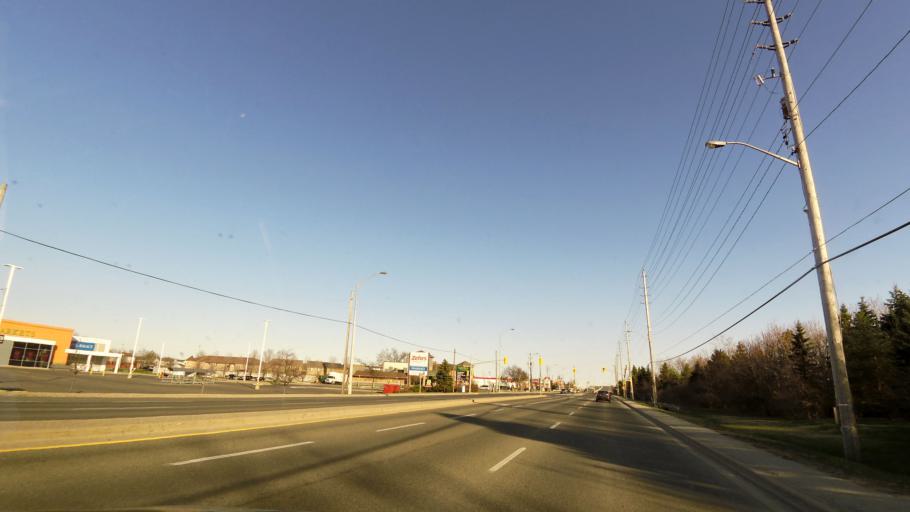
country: CA
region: Ontario
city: Brampton
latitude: 43.8713
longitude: -79.7267
